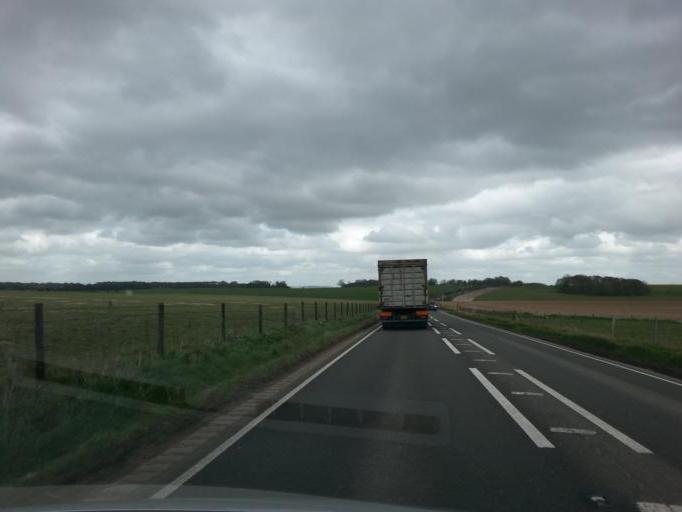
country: GB
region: England
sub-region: Wiltshire
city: Durnford
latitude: 51.1765
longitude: -1.8288
